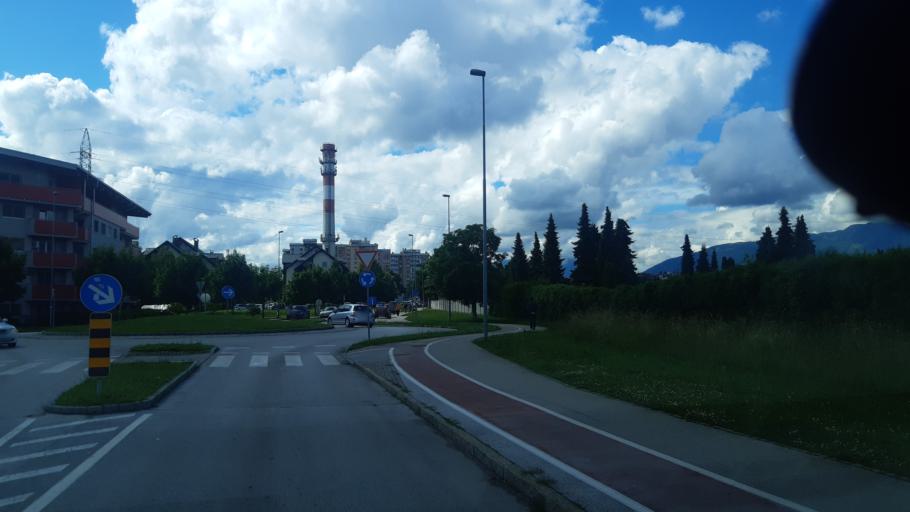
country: SI
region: Kranj
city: Kranj
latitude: 46.2331
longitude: 14.3685
